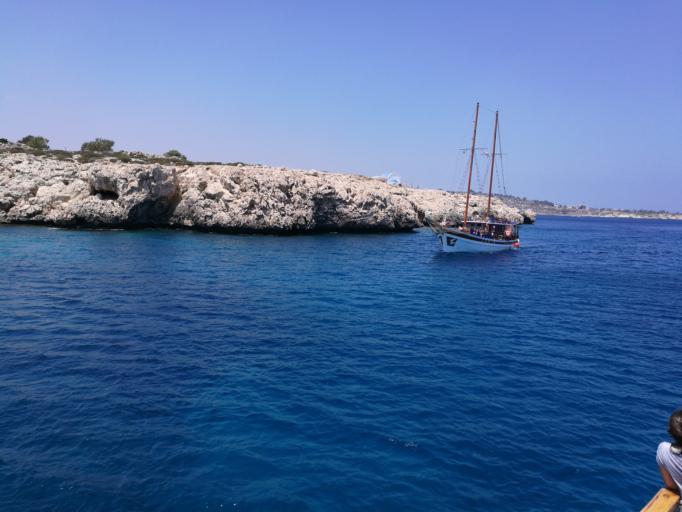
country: CY
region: Ammochostos
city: Protaras
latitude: 34.9742
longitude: 34.0773
